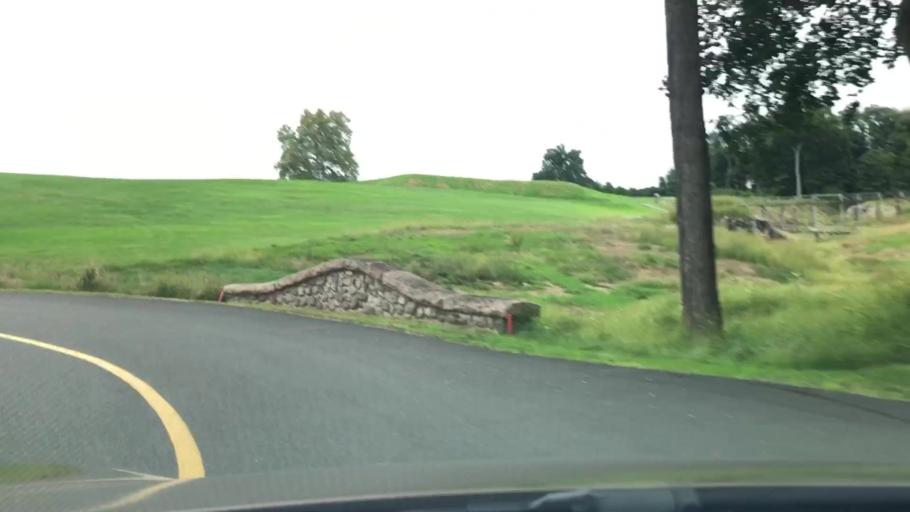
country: US
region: New York
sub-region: Westchester County
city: Ossining
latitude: 41.1293
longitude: -73.8561
